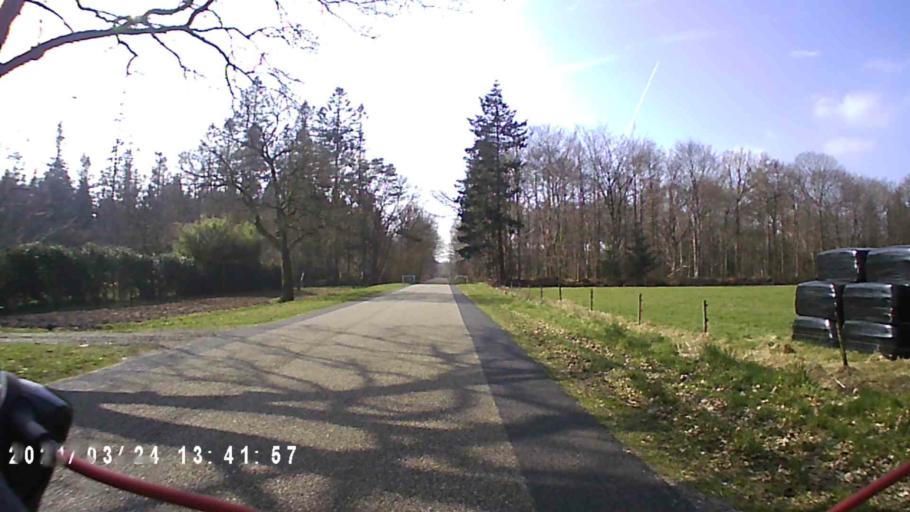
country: NL
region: Groningen
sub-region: Gemeente Leek
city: Leek
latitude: 53.0889
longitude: 6.2773
